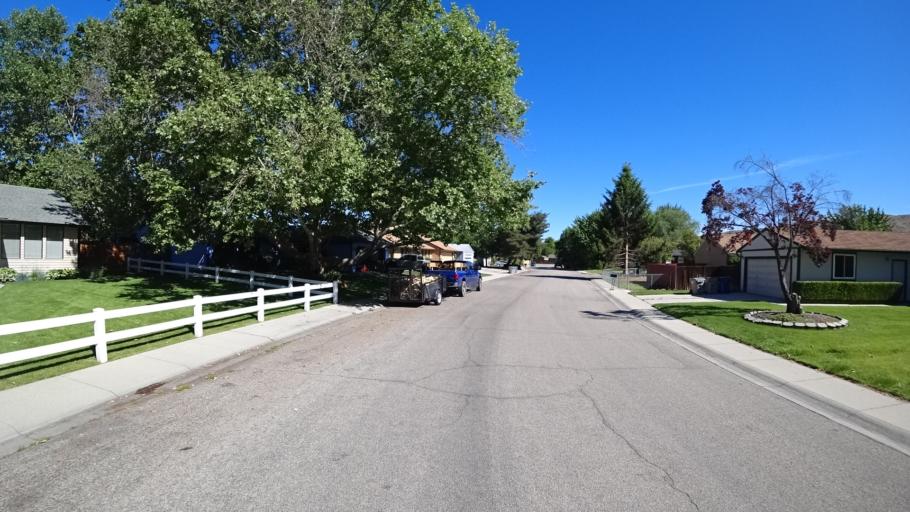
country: US
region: Idaho
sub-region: Ada County
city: Garden City
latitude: 43.6635
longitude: -116.2618
